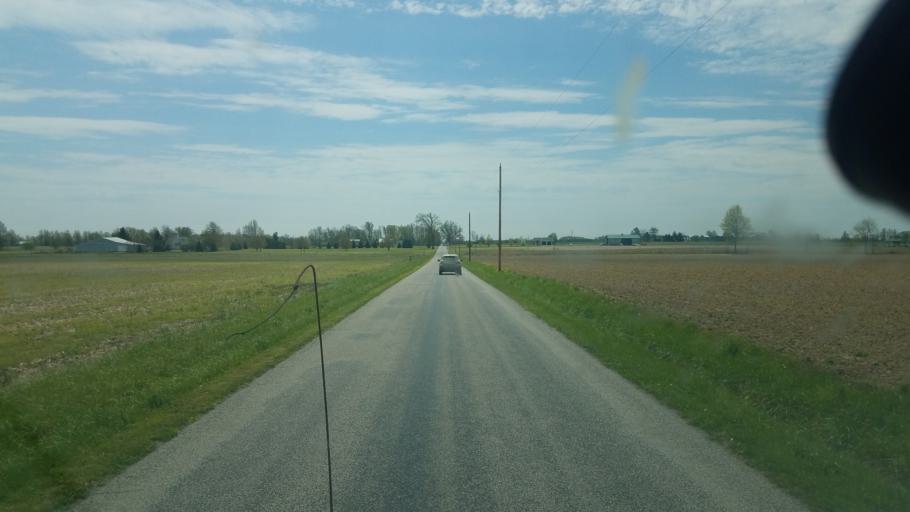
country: US
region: Ohio
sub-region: Allen County
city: Bluffton
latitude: 40.8070
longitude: -83.9088
